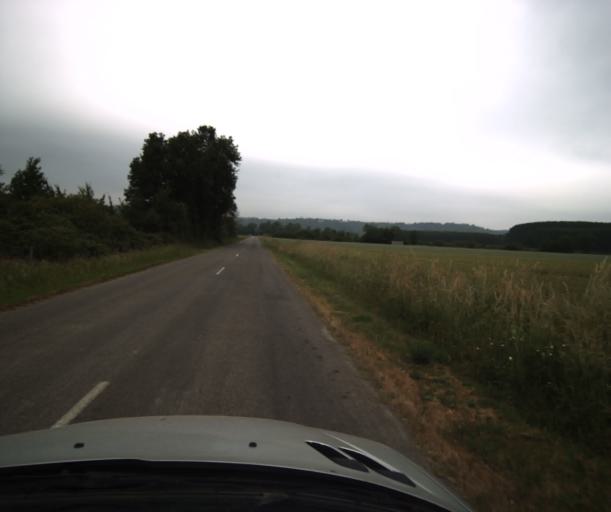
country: FR
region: Midi-Pyrenees
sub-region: Departement du Tarn-et-Garonne
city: Saint-Nicolas-de-la-Grave
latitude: 44.0780
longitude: 1.0253
